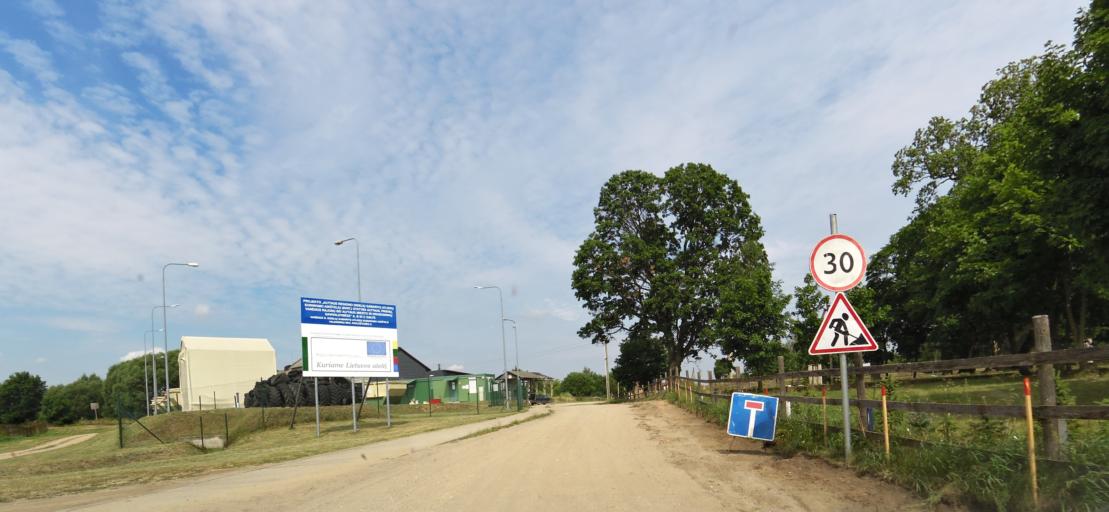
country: LT
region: Vilnius County
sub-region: Trakai
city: Rudiskes
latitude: 54.3533
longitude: 24.8288
